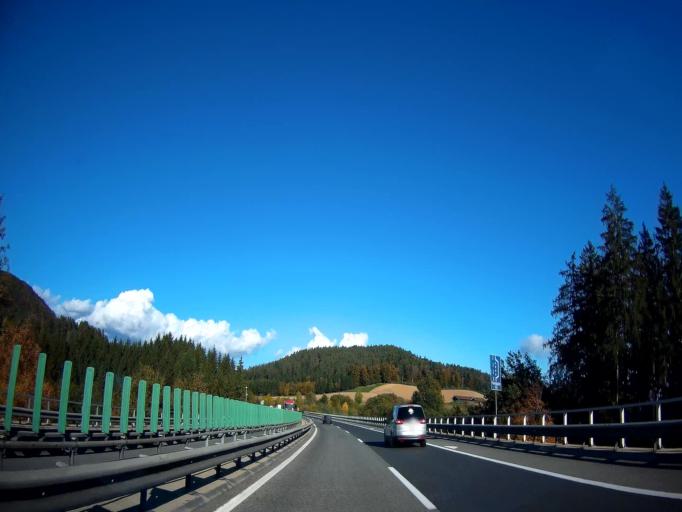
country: AT
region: Carinthia
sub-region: Politischer Bezirk Volkermarkt
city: Voelkermarkt
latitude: 46.6445
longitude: 14.5550
